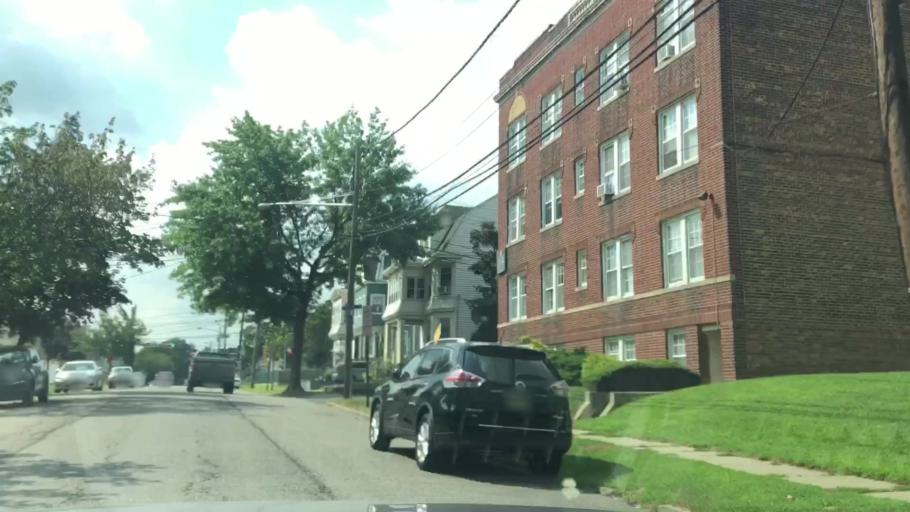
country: US
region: New Jersey
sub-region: Essex County
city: Bloomfield
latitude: 40.7901
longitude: -74.1860
